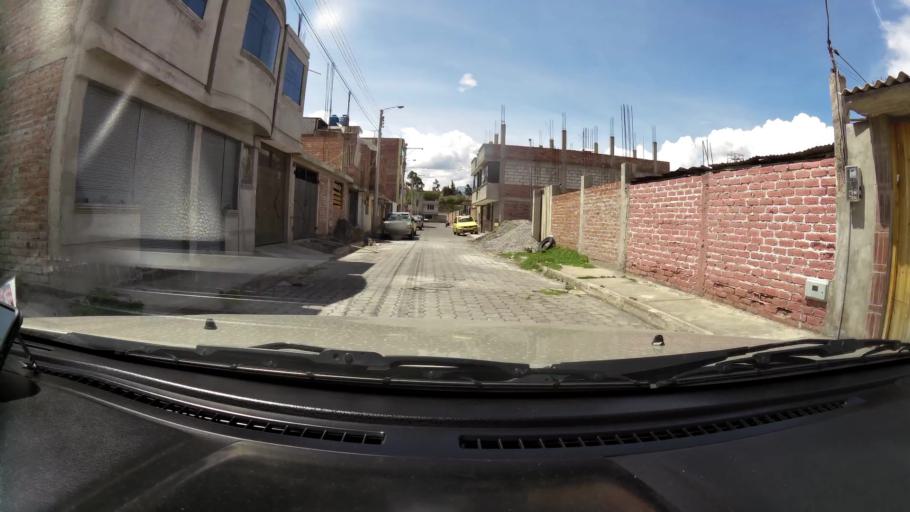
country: EC
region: Chimborazo
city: Riobamba
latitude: -1.6589
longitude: -78.6402
